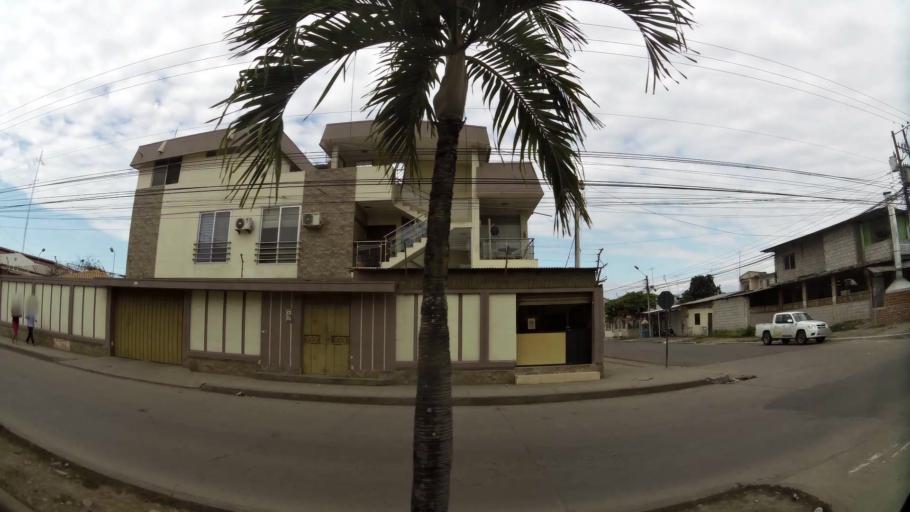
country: EC
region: El Oro
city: Machala
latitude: -3.2515
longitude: -79.9577
